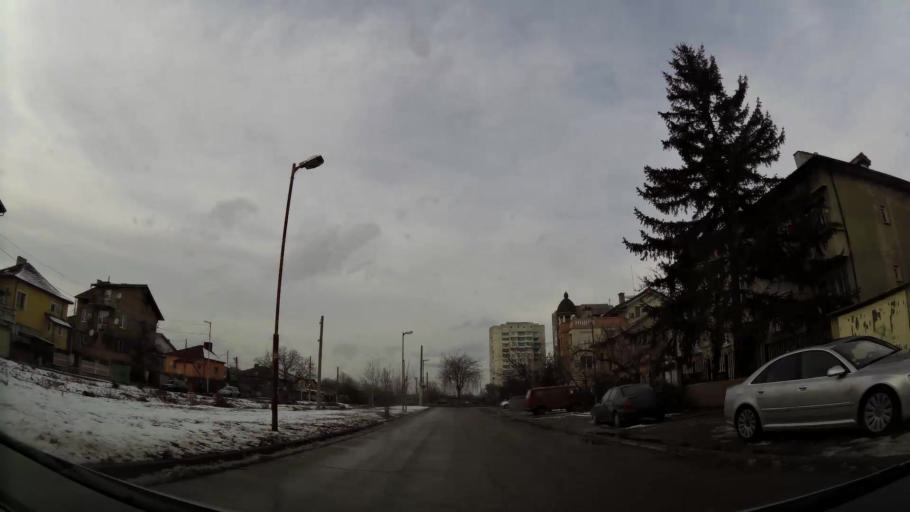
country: BG
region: Sofia-Capital
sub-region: Stolichna Obshtina
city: Sofia
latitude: 42.7064
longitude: 23.3764
